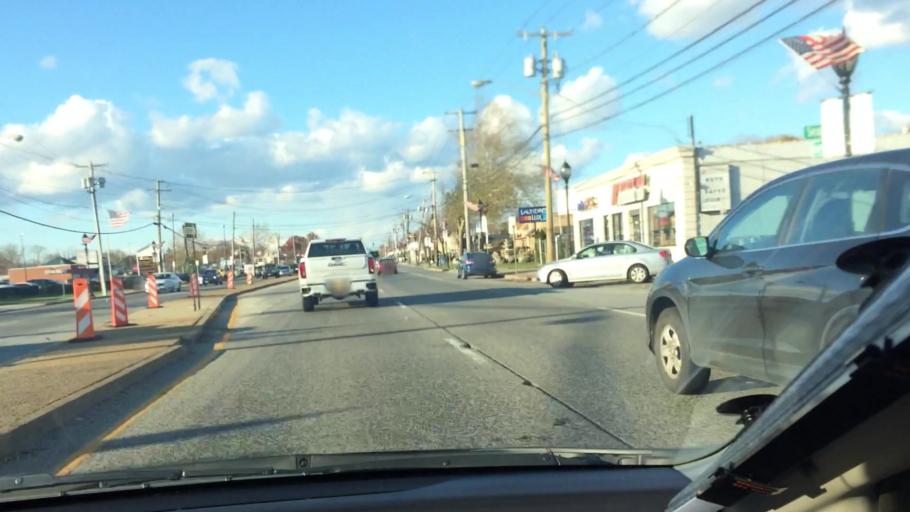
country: US
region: New York
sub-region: Suffolk County
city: Deer Park
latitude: 40.7624
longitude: -73.3296
